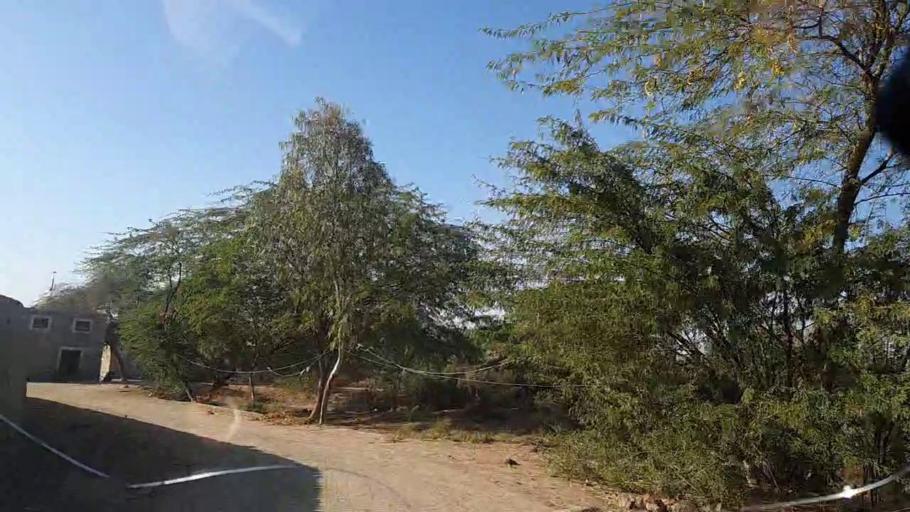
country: PK
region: Sindh
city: Khanpur
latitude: 27.7666
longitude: 69.2943
